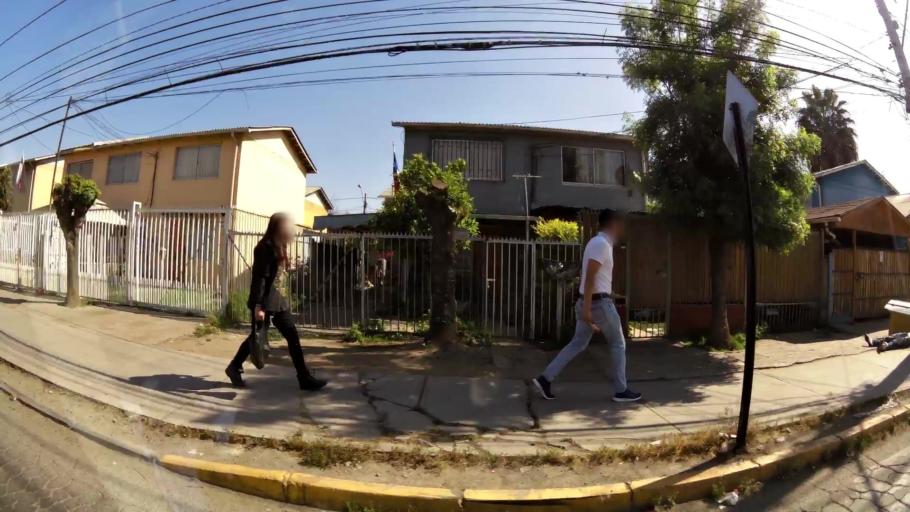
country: CL
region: Santiago Metropolitan
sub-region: Provincia de Santiago
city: Lo Prado
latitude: -33.3590
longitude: -70.7472
